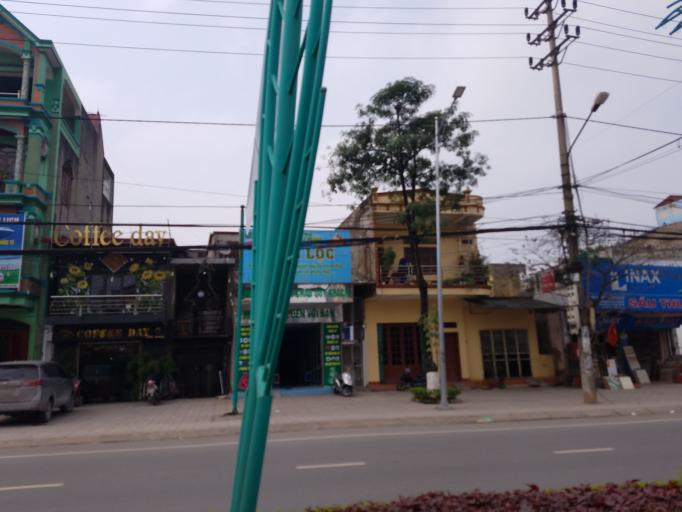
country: VN
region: Thai Nguyen
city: Thanh Pho Thai Nguyen
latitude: 21.5866
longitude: 105.8263
